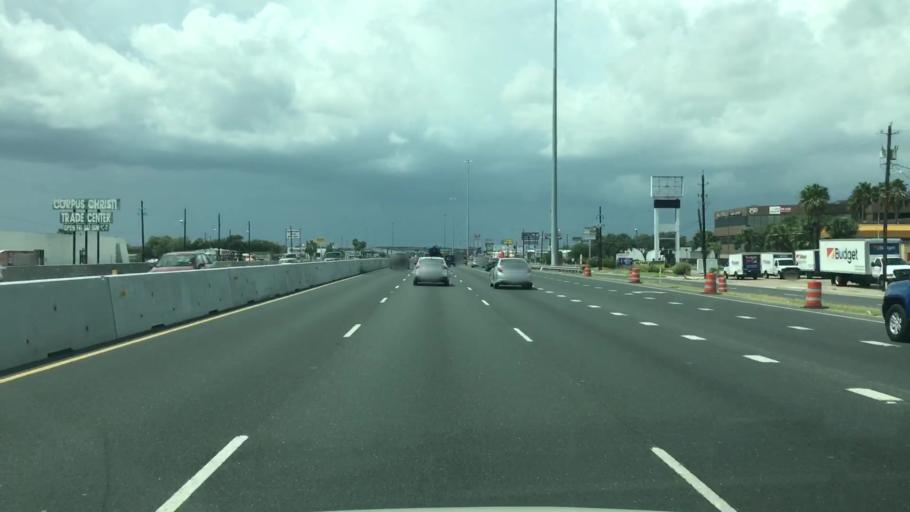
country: US
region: Texas
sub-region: Nueces County
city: Corpus Christi
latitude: 27.7309
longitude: -97.4174
